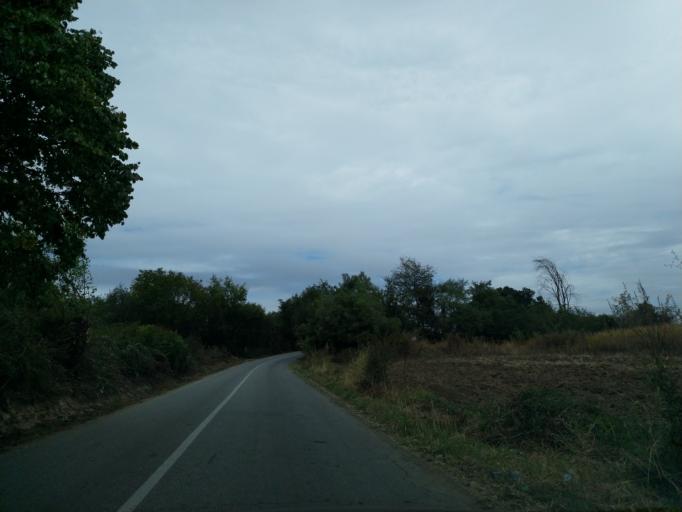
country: RS
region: Central Serbia
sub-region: Pomoravski Okrug
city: Paracin
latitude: 43.8506
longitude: 21.3226
